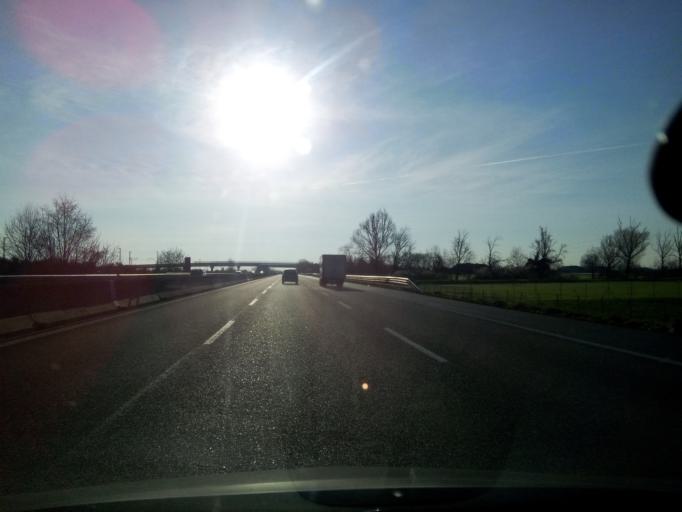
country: IT
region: Emilia-Romagna
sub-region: Provincia di Parma
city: Fontanellato
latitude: 44.8733
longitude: 10.1889
